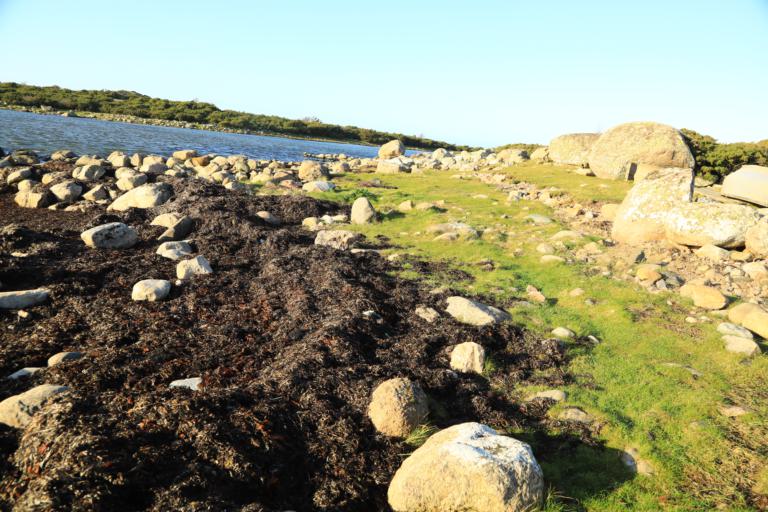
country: SE
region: Halland
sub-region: Varbergs Kommun
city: Varberg
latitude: 57.1644
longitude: 12.2129
